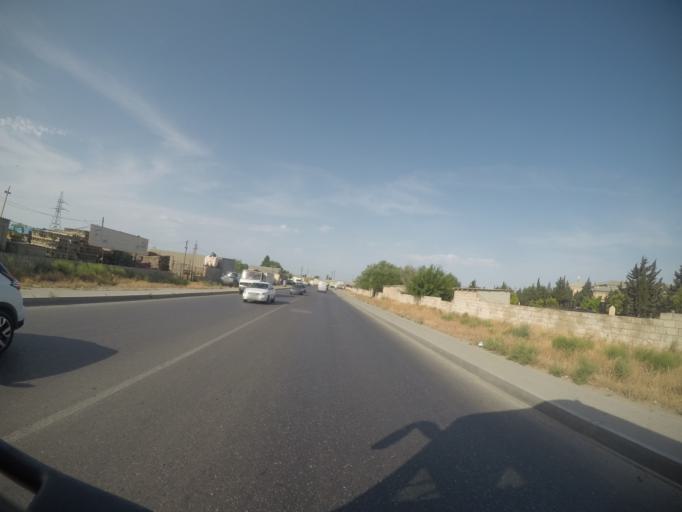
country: AZ
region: Baki
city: Bilajari
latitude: 40.4395
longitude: 49.7817
